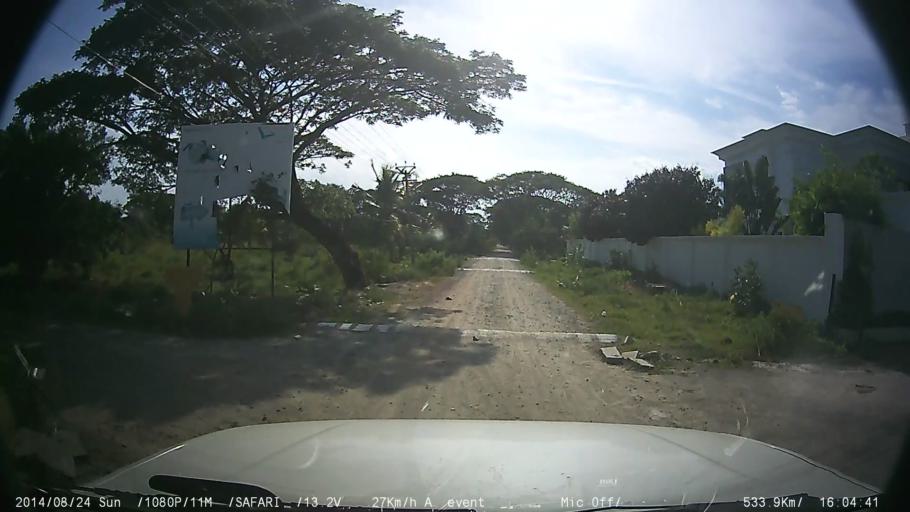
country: IN
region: Tamil Nadu
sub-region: Kancheepuram
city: Vengavasal
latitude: 12.8161
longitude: 80.2214
